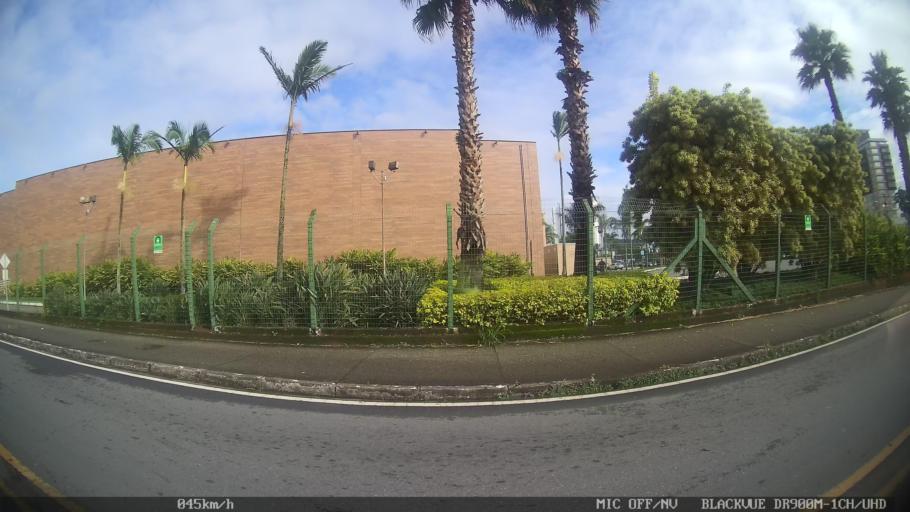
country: BR
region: Santa Catarina
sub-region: Sao Jose
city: Campinas
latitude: -27.5841
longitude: -48.6134
